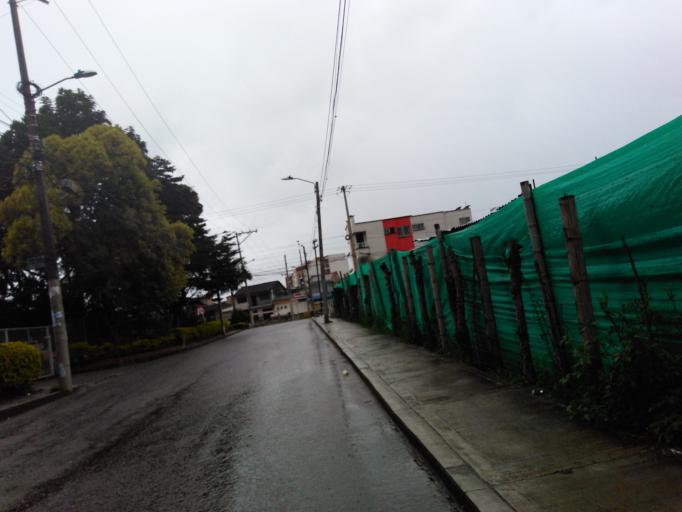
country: CO
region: Cauca
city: Popayan
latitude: 2.4524
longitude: -76.5944
